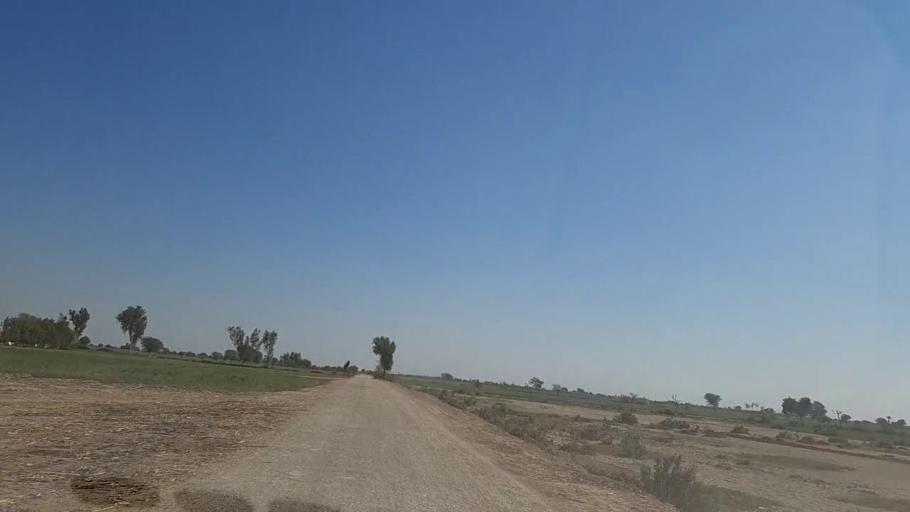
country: PK
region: Sindh
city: Digri
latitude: 25.1124
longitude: 69.1162
